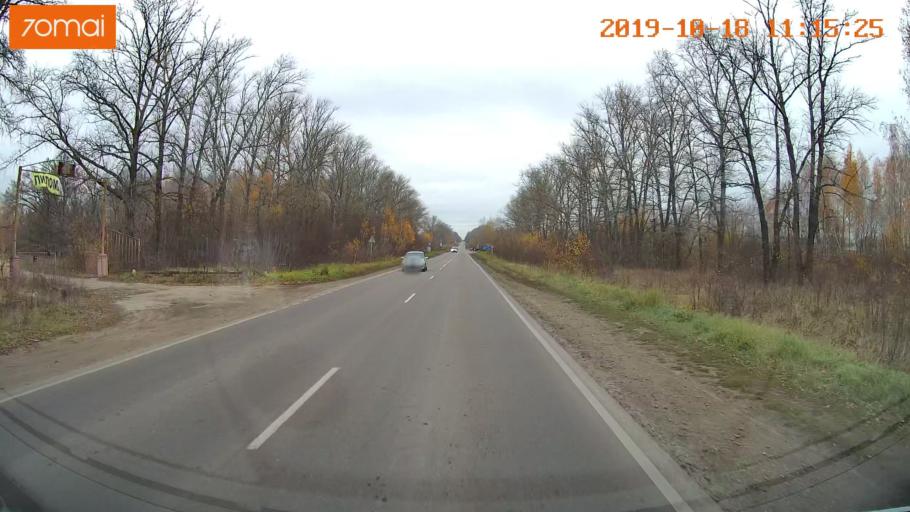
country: RU
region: Tula
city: Kimovsk
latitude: 53.9921
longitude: 38.5475
